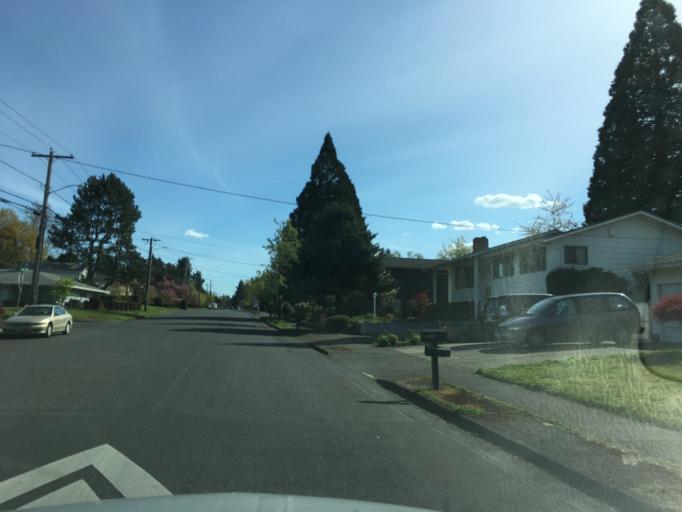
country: US
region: Oregon
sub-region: Multnomah County
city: Lents
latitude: 45.5428
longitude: -122.5271
